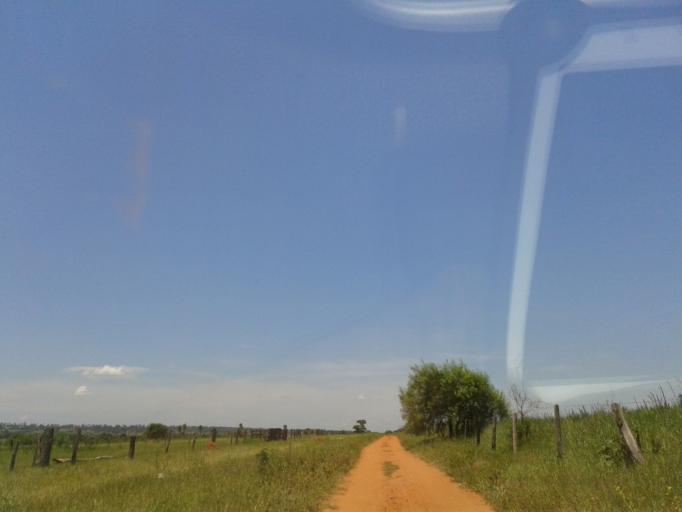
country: BR
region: Minas Gerais
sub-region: Santa Vitoria
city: Santa Vitoria
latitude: -19.2203
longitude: -50.4337
